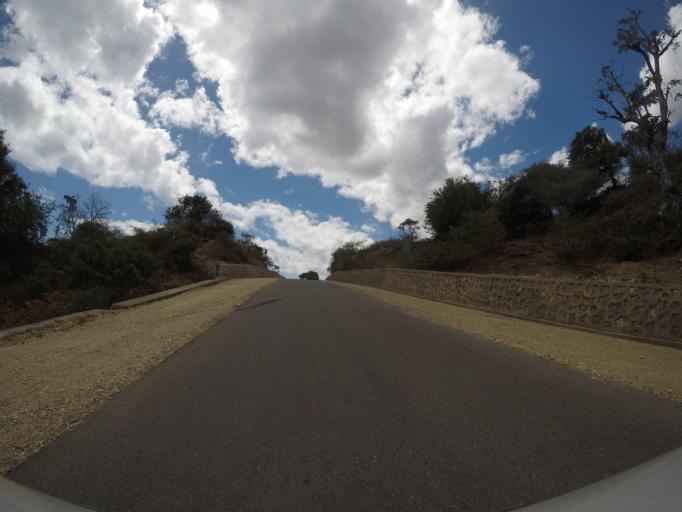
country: TL
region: Lautem
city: Lospalos
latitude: -8.3526
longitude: 126.9214
